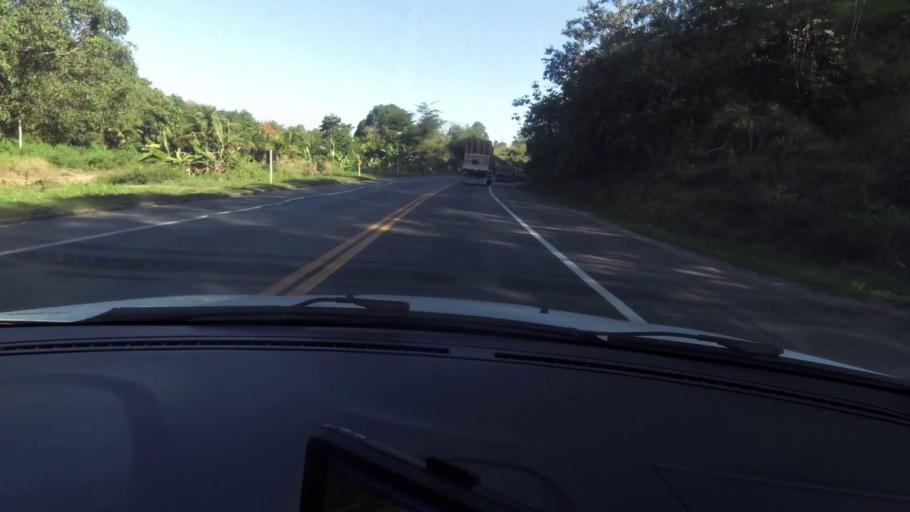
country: BR
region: Espirito Santo
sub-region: Alfredo Chaves
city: Alfredo Chaves
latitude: -20.6823
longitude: -40.6682
